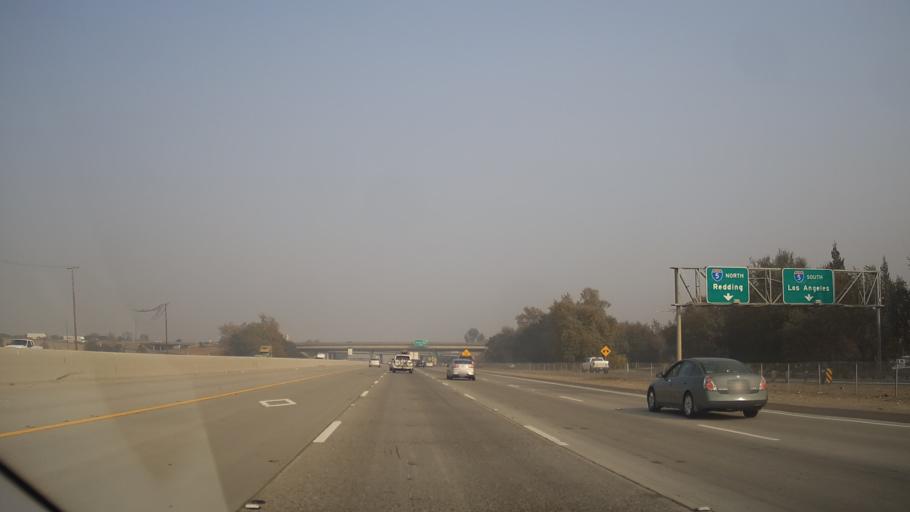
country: US
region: California
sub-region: Yolo County
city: West Sacramento
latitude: 38.6226
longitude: -121.5215
